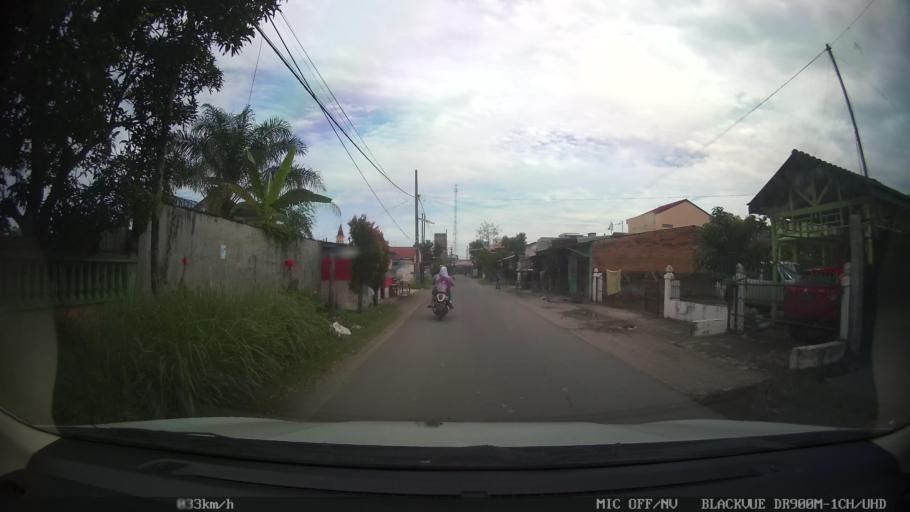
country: ID
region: North Sumatra
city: Sunggal
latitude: 3.5973
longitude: 98.5661
